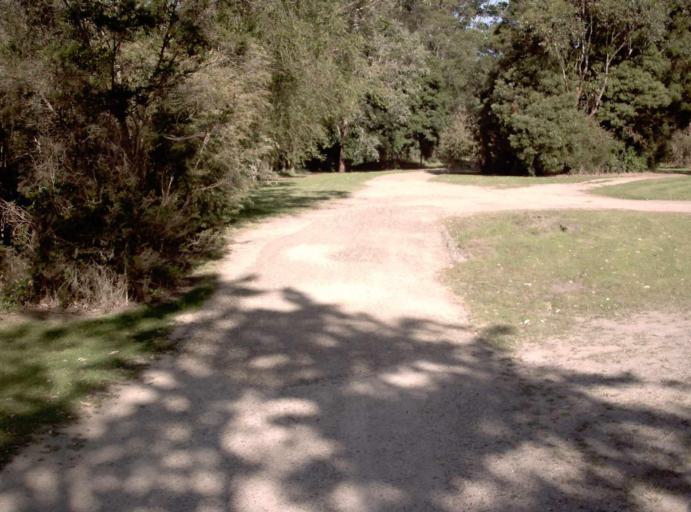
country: AU
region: Victoria
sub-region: East Gippsland
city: Lakes Entrance
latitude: -37.7134
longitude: 148.4537
